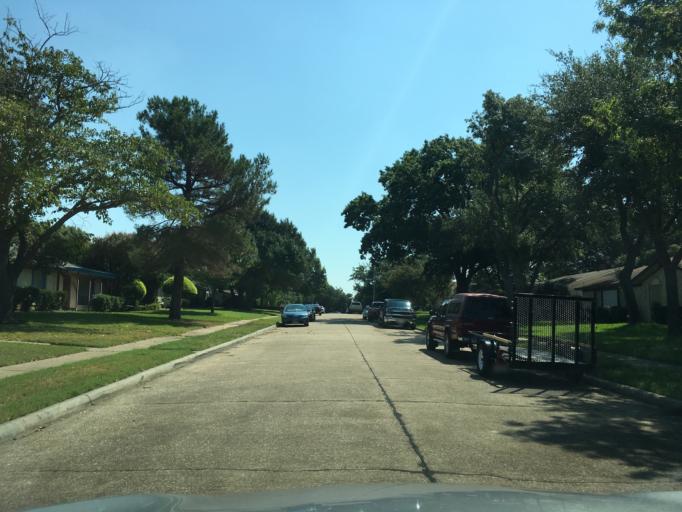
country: US
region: Texas
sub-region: Dallas County
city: Garland
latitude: 32.9322
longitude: -96.6549
